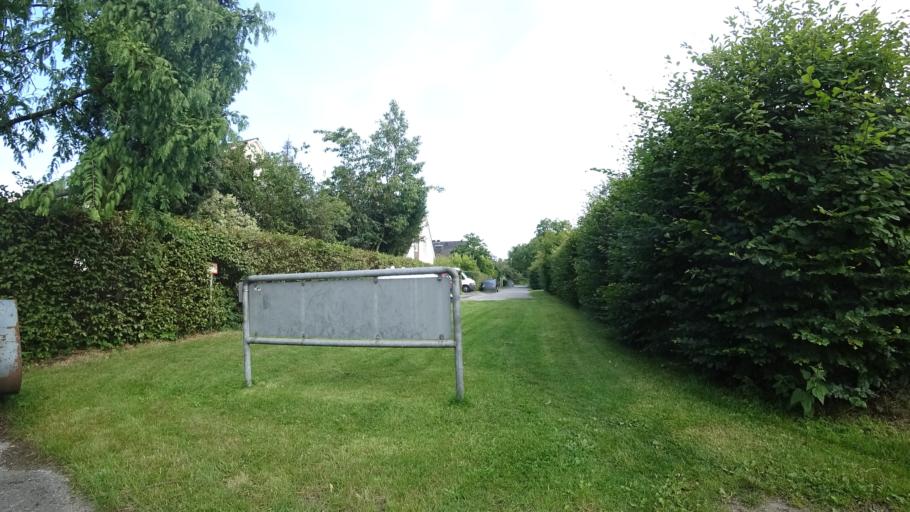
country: DE
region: North Rhine-Westphalia
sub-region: Regierungsbezirk Detmold
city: Guetersloh
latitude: 51.9395
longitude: 8.4323
